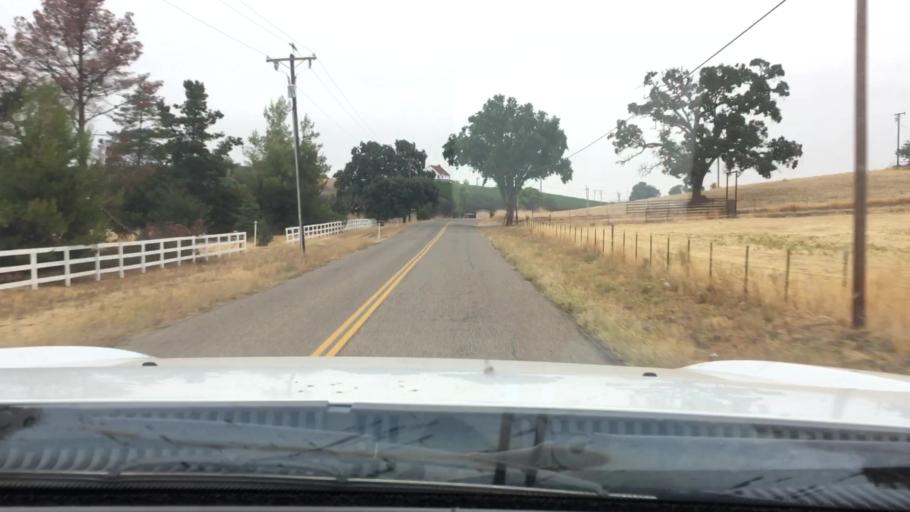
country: US
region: California
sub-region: San Luis Obispo County
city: Atascadero
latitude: 35.5344
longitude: -120.6140
